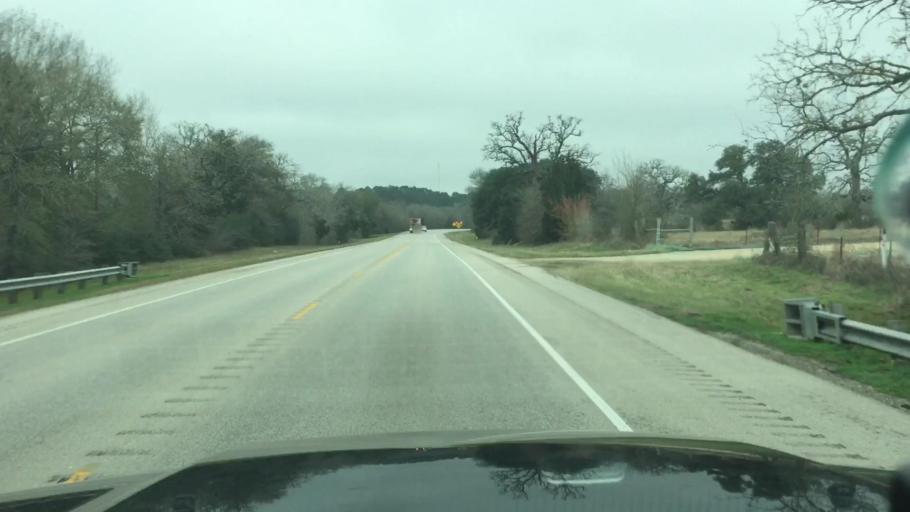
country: US
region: Texas
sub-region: Fayette County
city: La Grange
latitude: 30.0303
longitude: -96.9067
